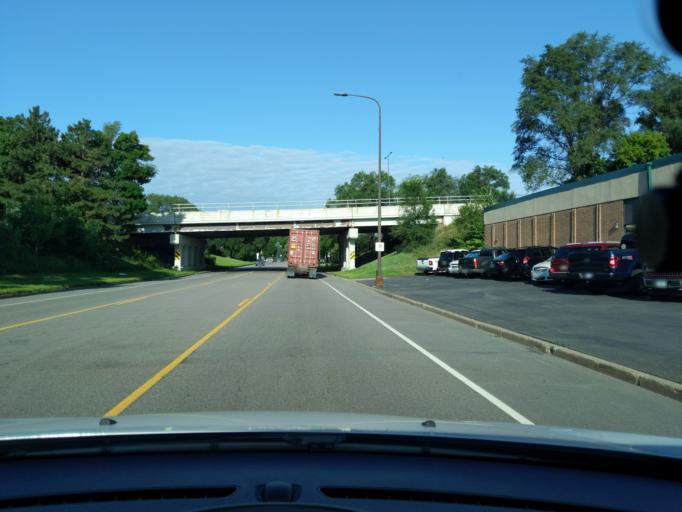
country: US
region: Minnesota
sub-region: Ramsey County
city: Falcon Heights
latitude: 44.9665
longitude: -93.1457
